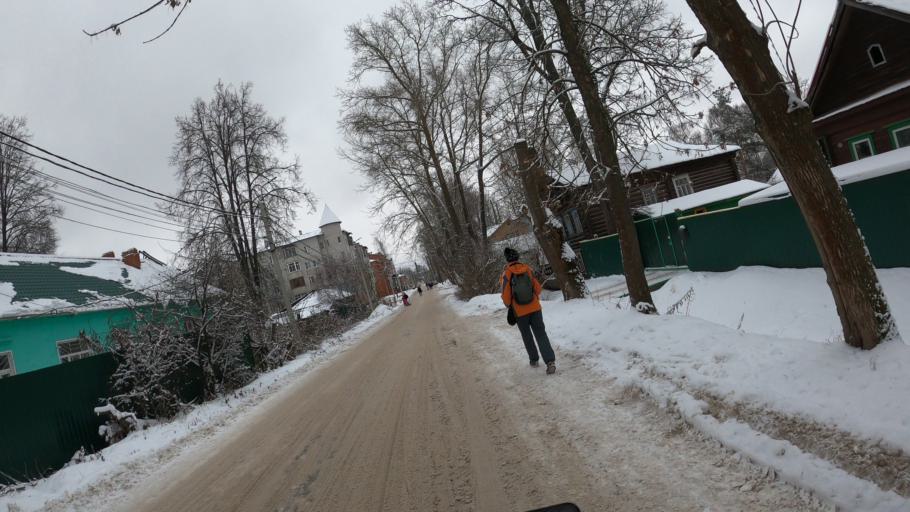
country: RU
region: Jaroslavl
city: Pereslavl'-Zalesskiy
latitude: 56.7443
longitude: 38.8625
